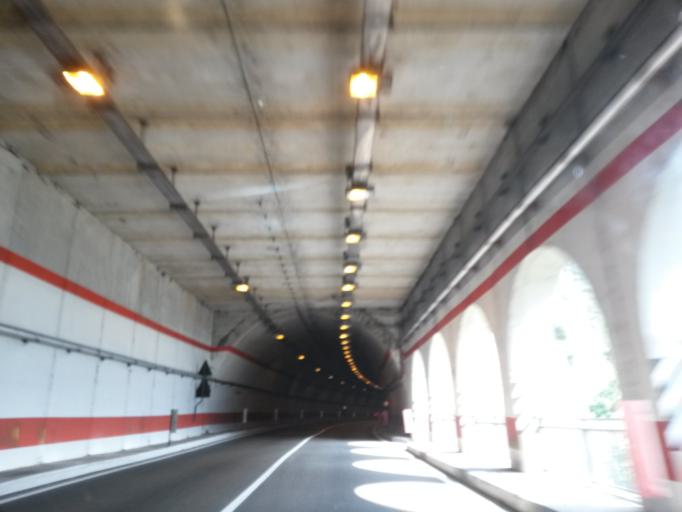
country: IT
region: Lombardy
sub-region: Provincia di Brescia
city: Gardola
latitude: 45.7379
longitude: 10.7356
